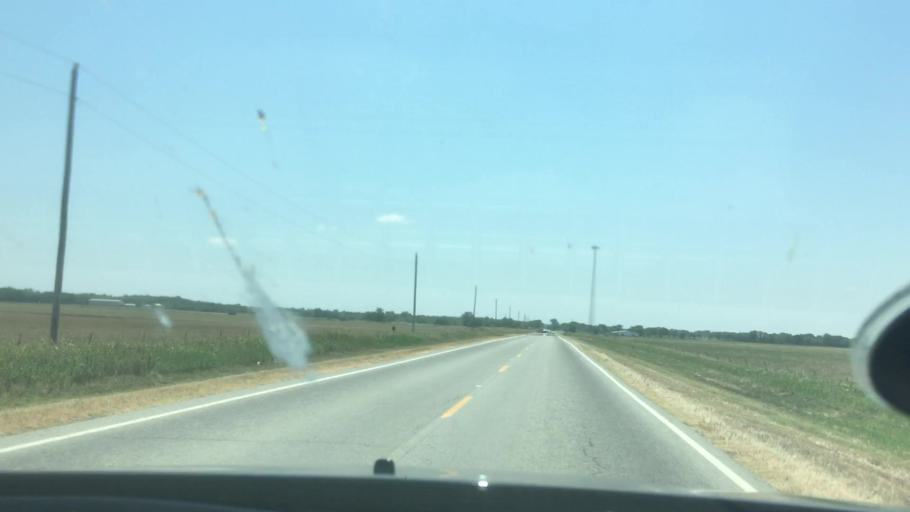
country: US
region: Oklahoma
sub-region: Coal County
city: Coalgate
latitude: 34.5112
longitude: -96.4070
